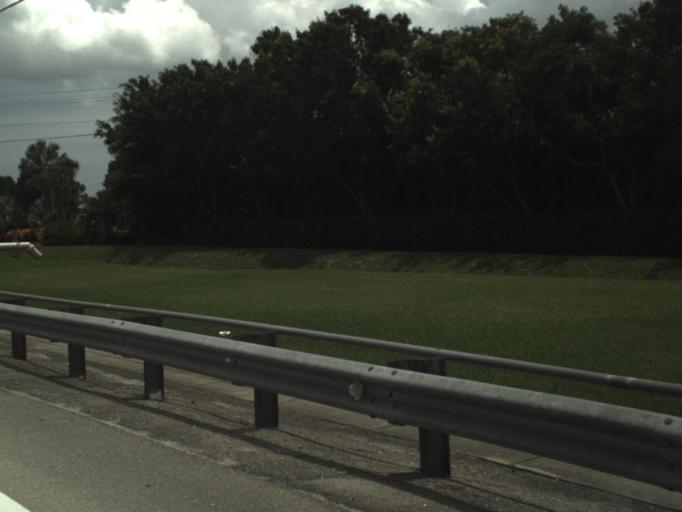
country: US
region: Florida
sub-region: Palm Beach County
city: Villages of Oriole
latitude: 26.4537
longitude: -80.1641
